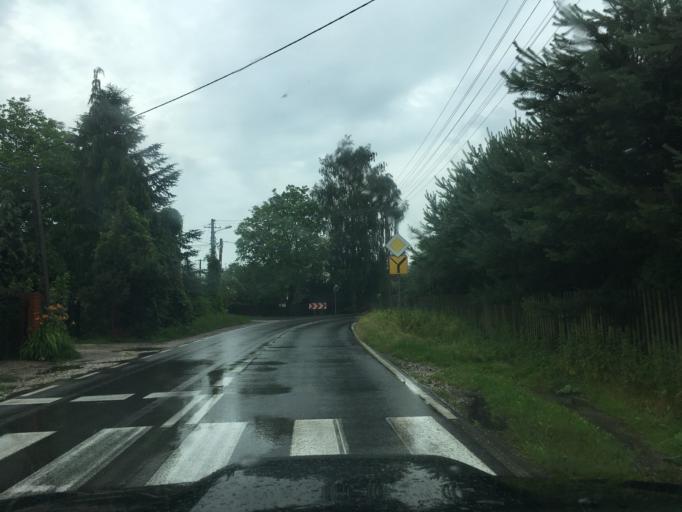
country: PL
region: Masovian Voivodeship
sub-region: Powiat piaseczynski
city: Gora Kalwaria
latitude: 51.9823
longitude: 21.2669
